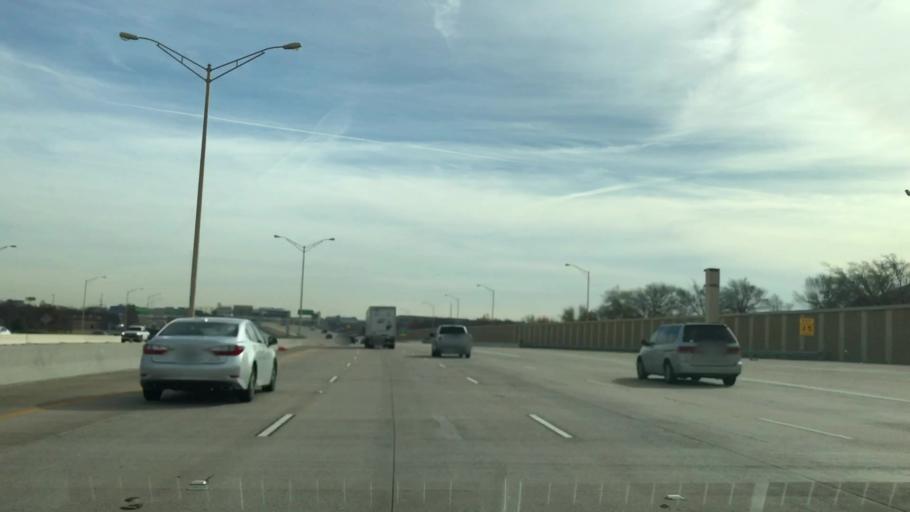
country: US
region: Texas
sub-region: Dallas County
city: Addison
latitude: 33.0009
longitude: -96.7737
